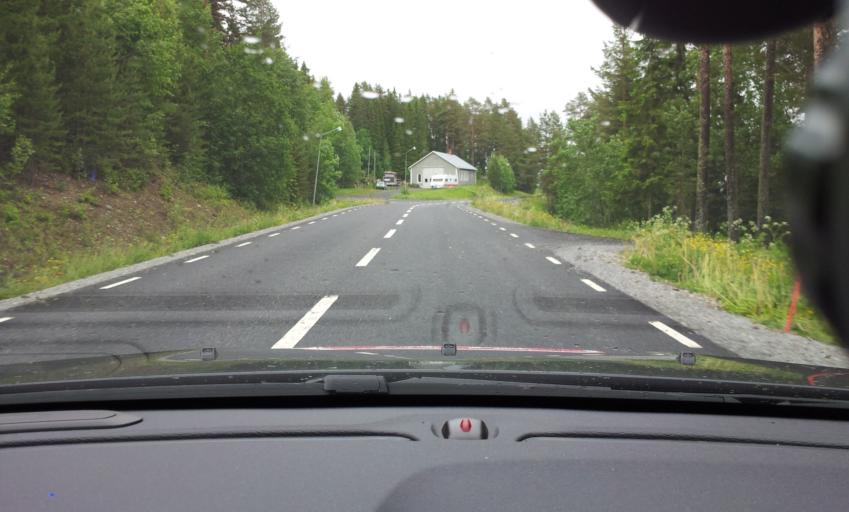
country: SE
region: Jaemtland
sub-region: OEstersunds Kommun
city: Lit
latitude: 63.7371
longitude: 14.8668
